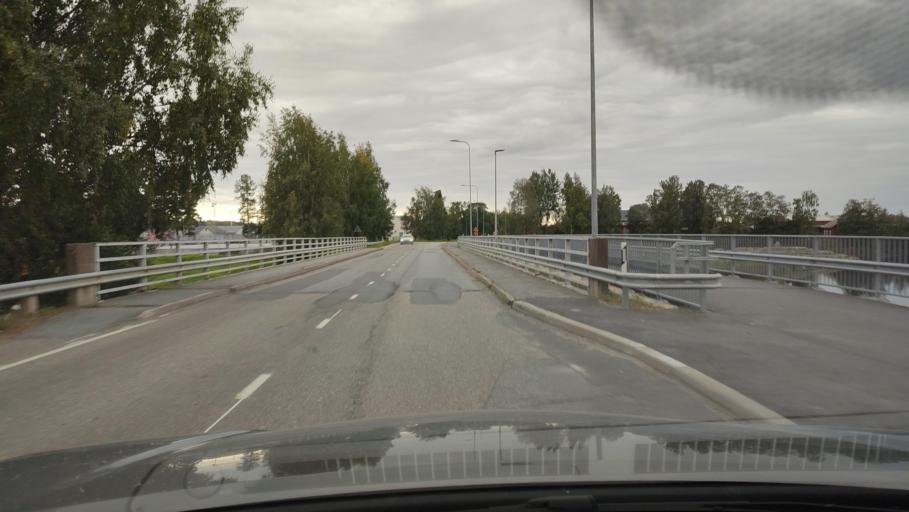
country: FI
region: Ostrobothnia
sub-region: Sydosterbotten
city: Kristinestad
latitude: 62.2564
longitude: 21.5265
